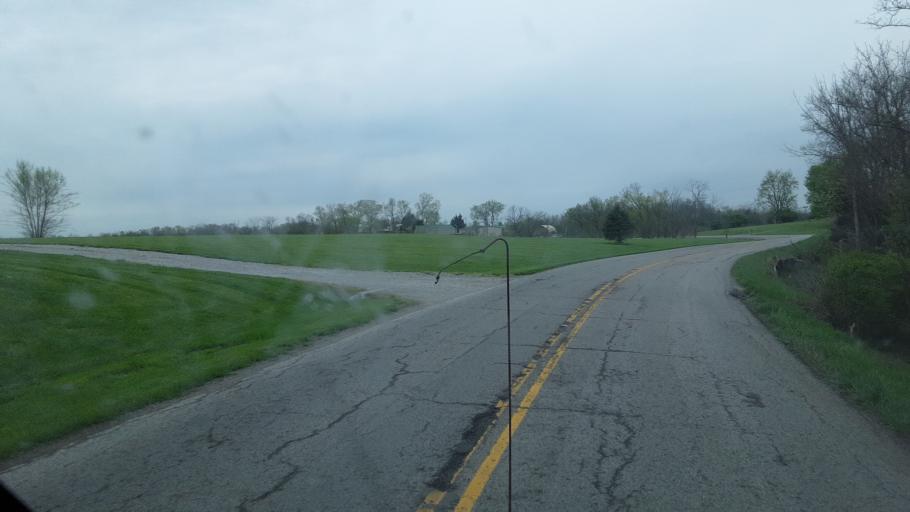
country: US
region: Kentucky
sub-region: Grant County
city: Dry Ridge
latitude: 38.6587
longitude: -84.6924
